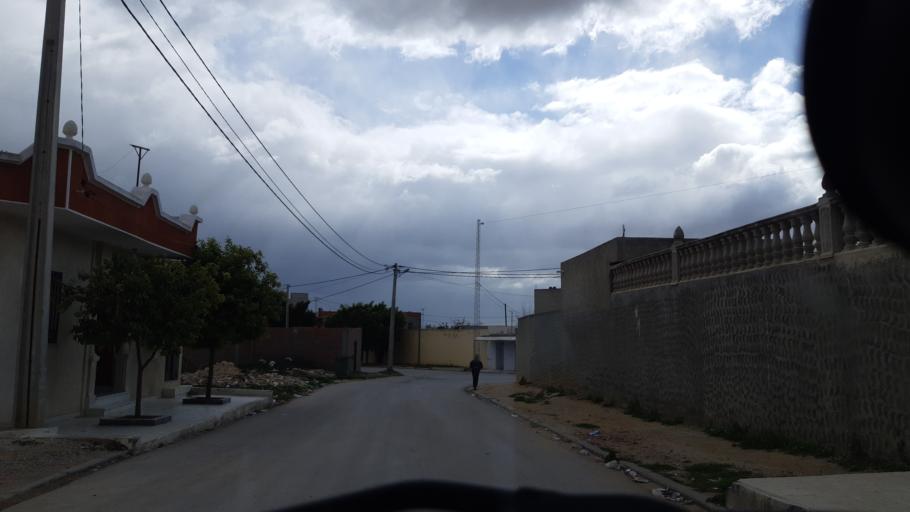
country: TN
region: Susah
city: Akouda
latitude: 35.8678
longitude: 10.5217
